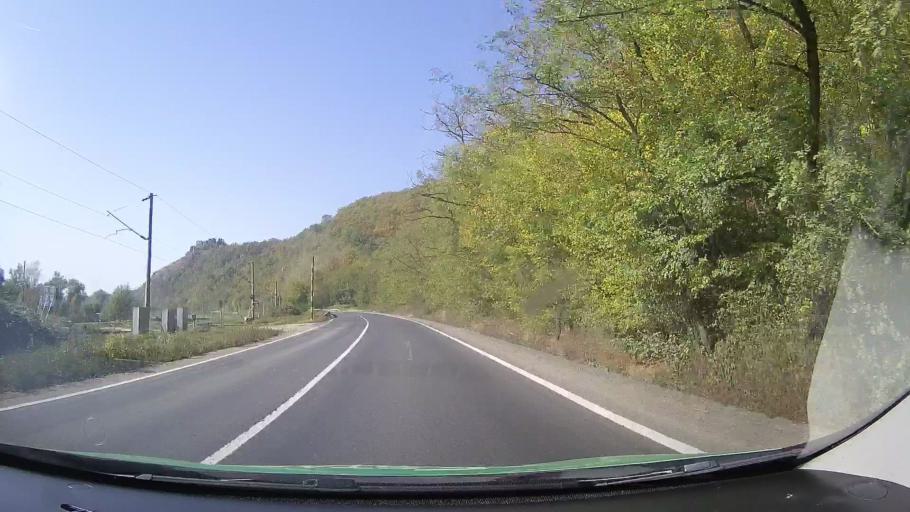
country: RO
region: Arad
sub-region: Oras Lipova
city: Lipova
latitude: 46.1088
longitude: 21.7349
